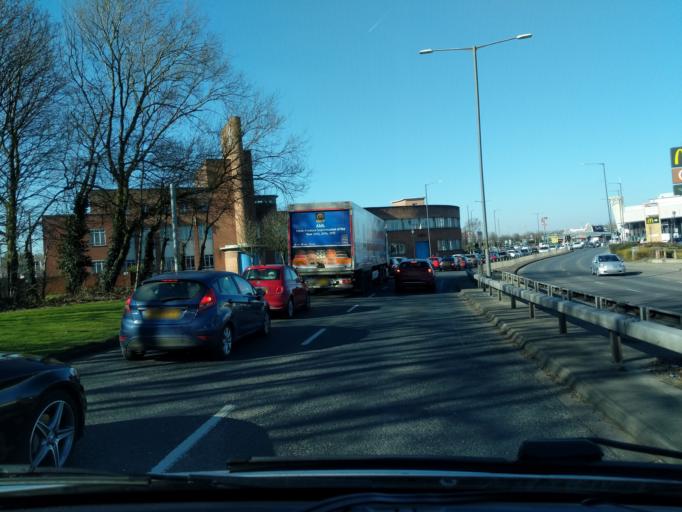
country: GB
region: England
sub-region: St. Helens
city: St Helens
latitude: 53.4499
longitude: -2.7394
